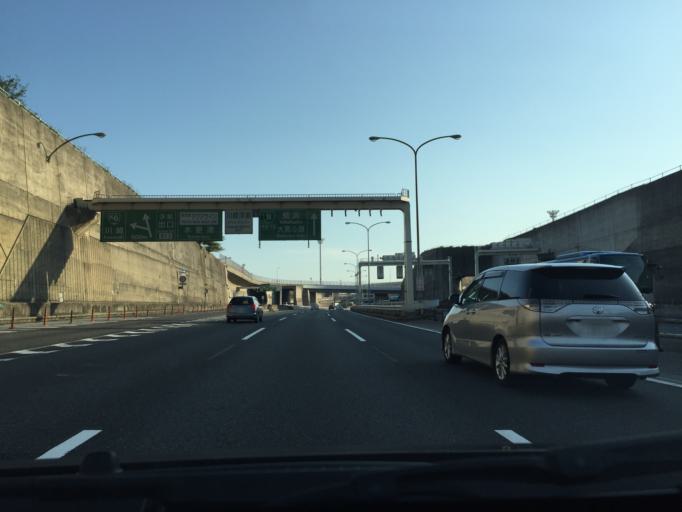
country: JP
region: Kanagawa
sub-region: Kawasaki-shi
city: Kawasaki
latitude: 35.5167
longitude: 139.7906
